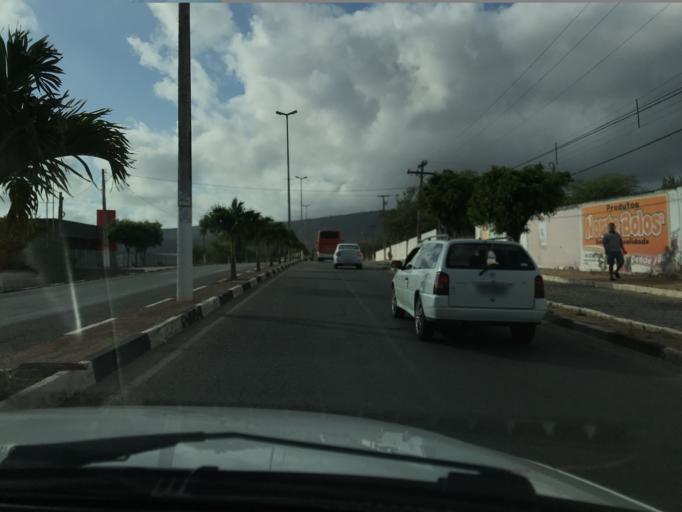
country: BR
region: Pernambuco
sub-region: Bezerros
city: Bezerros
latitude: -8.2330
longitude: -35.7445
